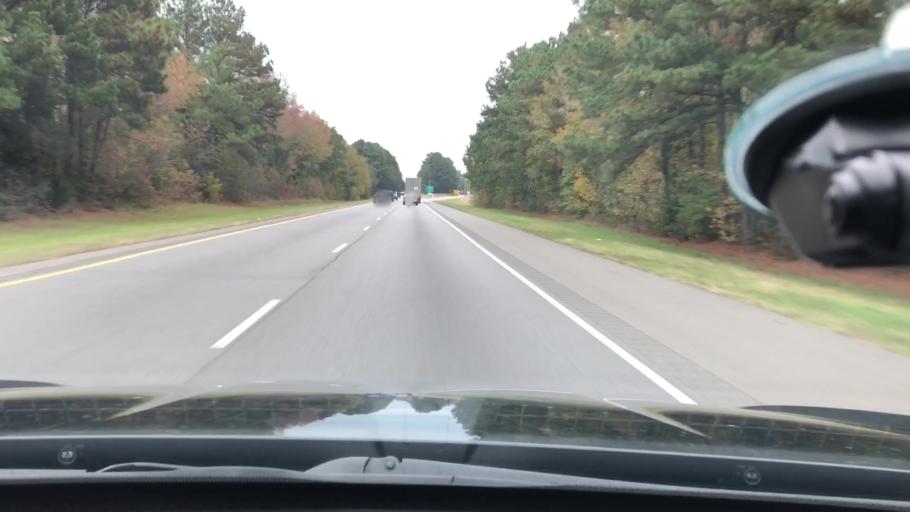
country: US
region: Arkansas
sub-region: Hempstead County
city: Hope
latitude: 33.6474
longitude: -93.6785
